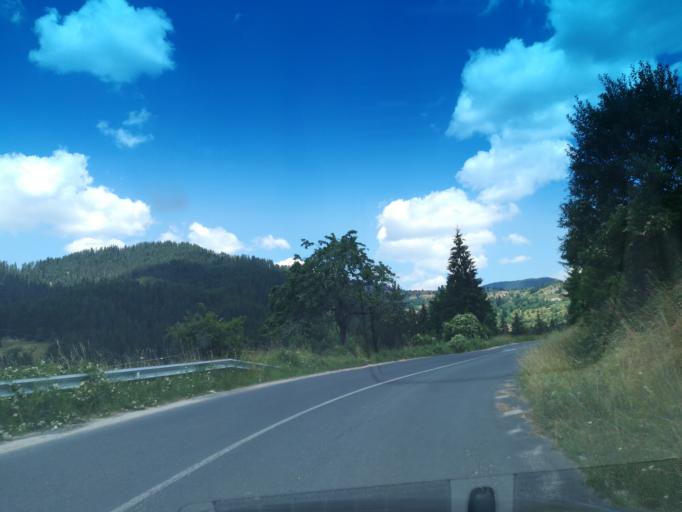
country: BG
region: Smolyan
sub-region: Obshtina Smolyan
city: Smolyan
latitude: 41.6576
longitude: 24.7675
